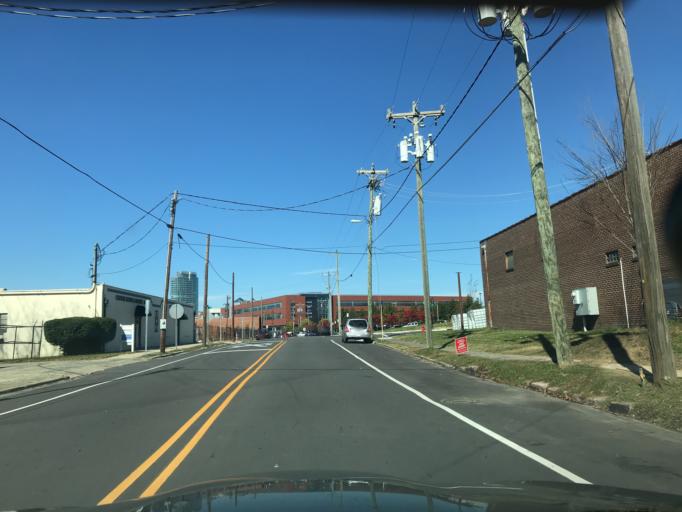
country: US
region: North Carolina
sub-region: Durham County
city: Durham
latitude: 35.9893
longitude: -78.8954
